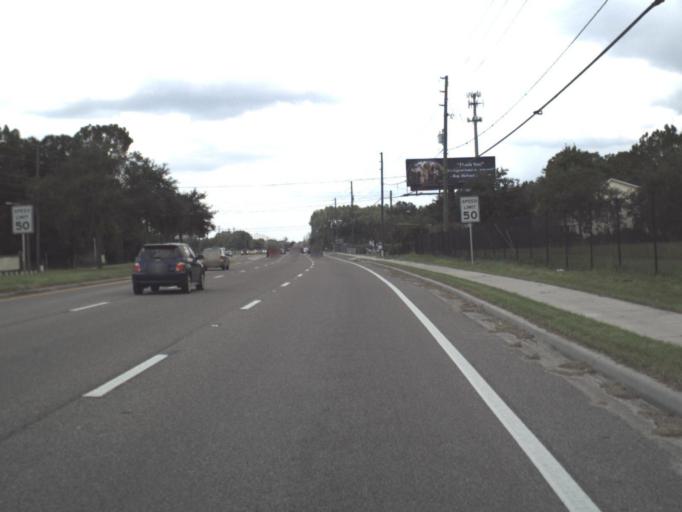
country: US
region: Florida
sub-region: Pasco County
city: Land O' Lakes
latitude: 28.2277
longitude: -82.4577
